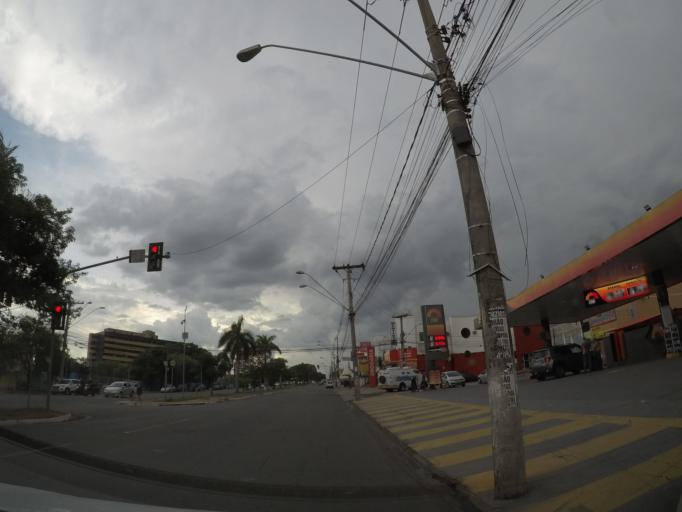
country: BR
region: Sao Paulo
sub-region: Sumare
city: Sumare
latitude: -22.8147
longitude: -47.2399
